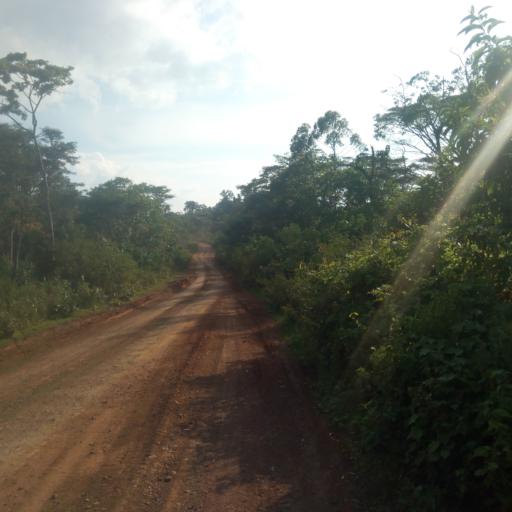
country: ET
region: Oromiya
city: Gore
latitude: 7.8910
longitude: 35.4868
